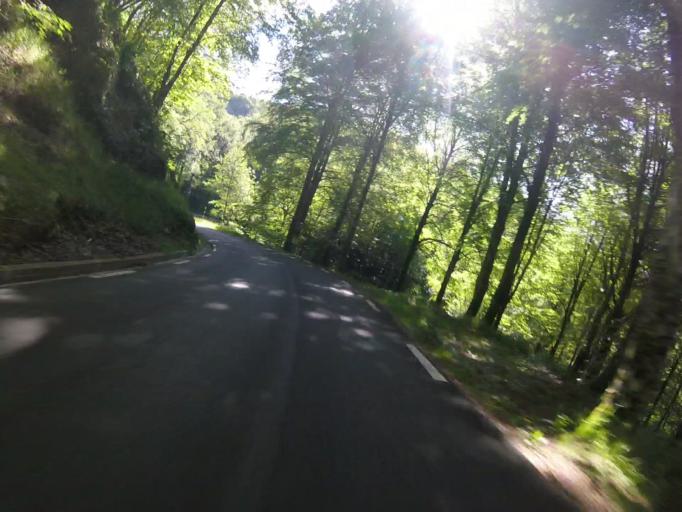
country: ES
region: Basque Country
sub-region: Provincia de Guipuzcoa
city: Albiztur
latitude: 43.1247
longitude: -2.1671
